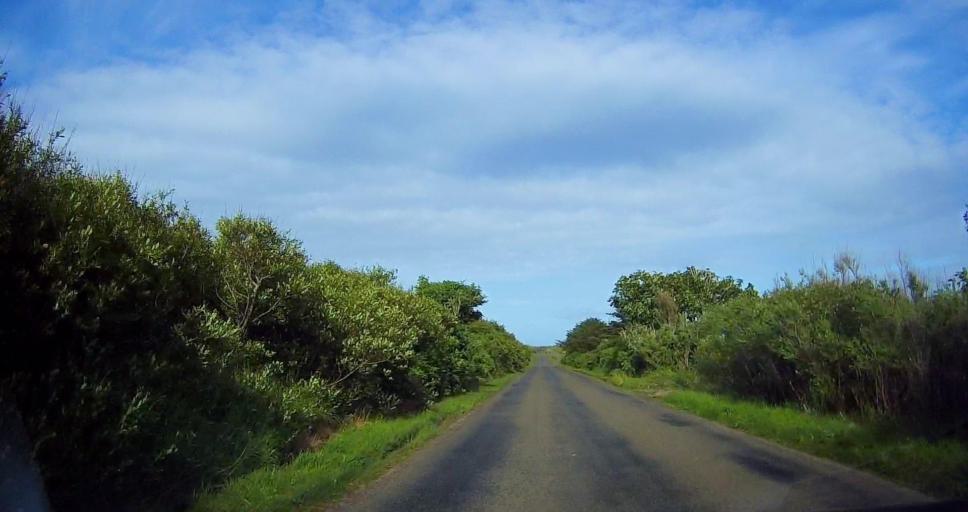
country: GB
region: Scotland
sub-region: Orkney Islands
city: Stromness
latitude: 58.8030
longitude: -3.2339
